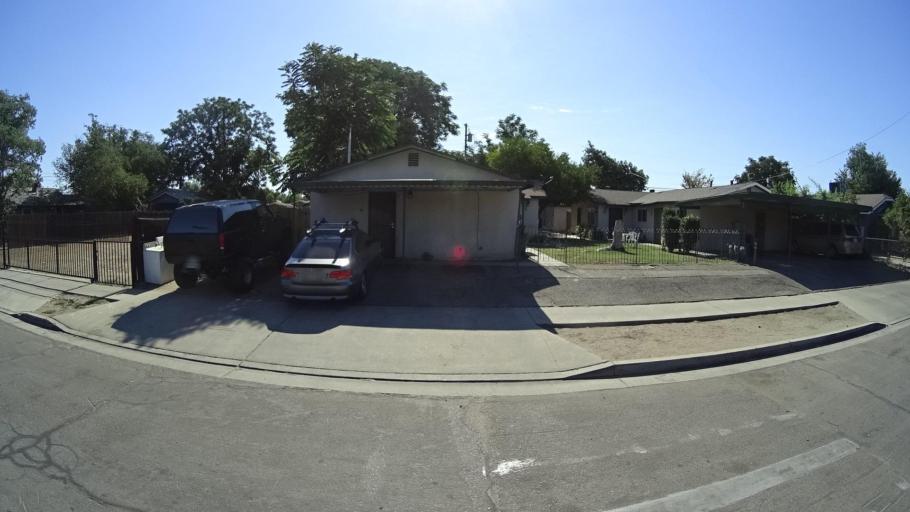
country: US
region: California
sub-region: Fresno County
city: Fresno
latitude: 36.7350
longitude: -119.7523
